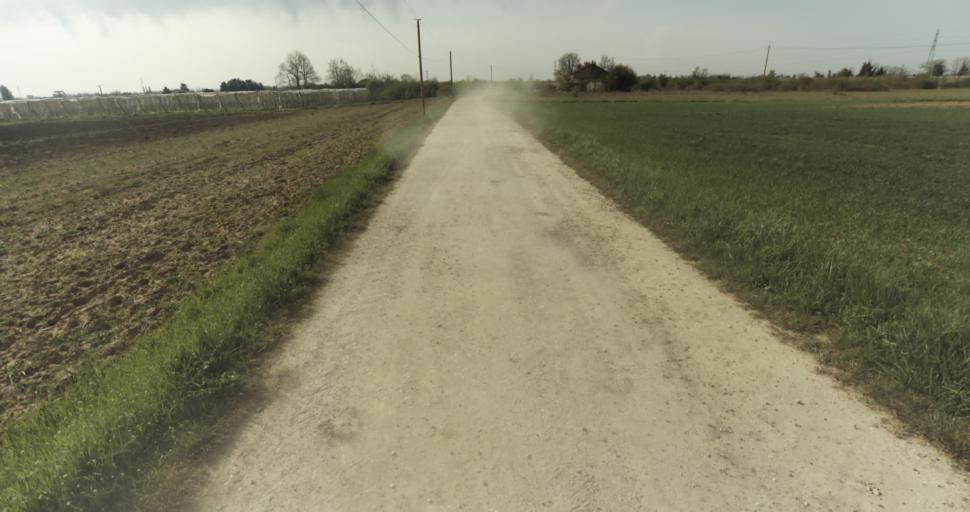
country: FR
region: Midi-Pyrenees
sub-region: Departement du Tarn-et-Garonne
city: Moissac
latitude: 44.1136
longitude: 1.1318
